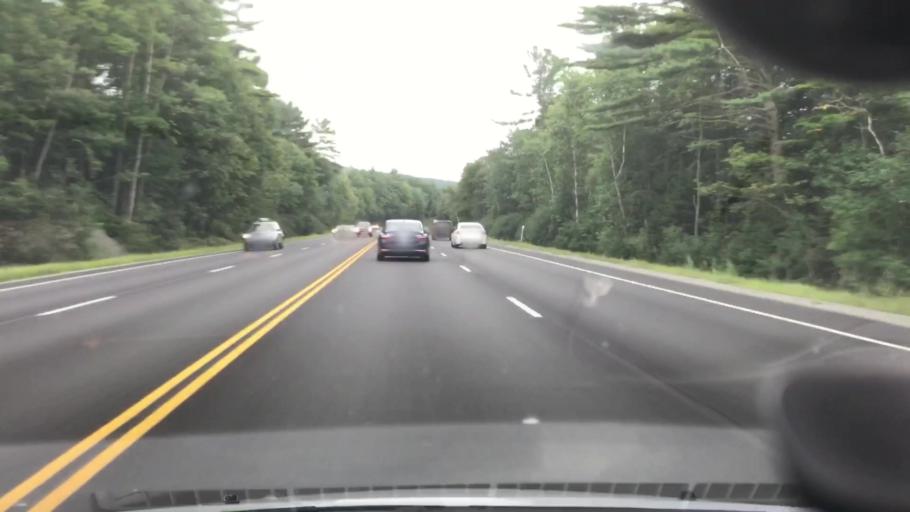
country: US
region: New Hampshire
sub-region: Grafton County
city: Lebanon
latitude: 43.6682
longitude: -72.2521
